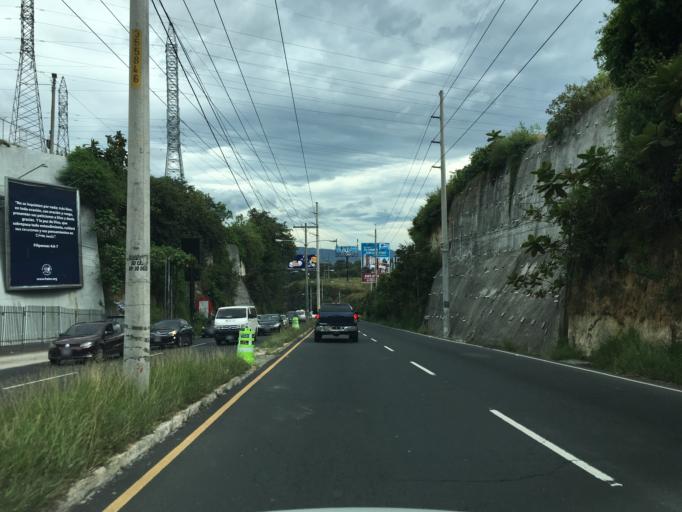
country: GT
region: Guatemala
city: Mixco
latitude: 14.5912
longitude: -90.5769
